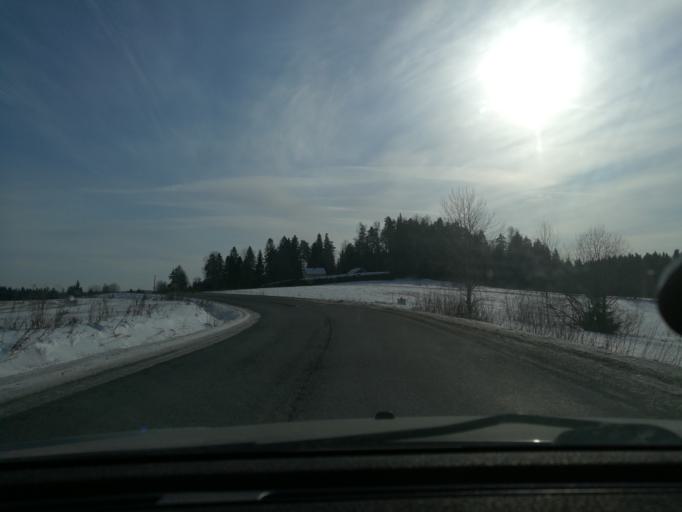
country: FI
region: Uusimaa
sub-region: Helsinki
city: Saukkola
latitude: 60.4973
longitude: 23.9589
